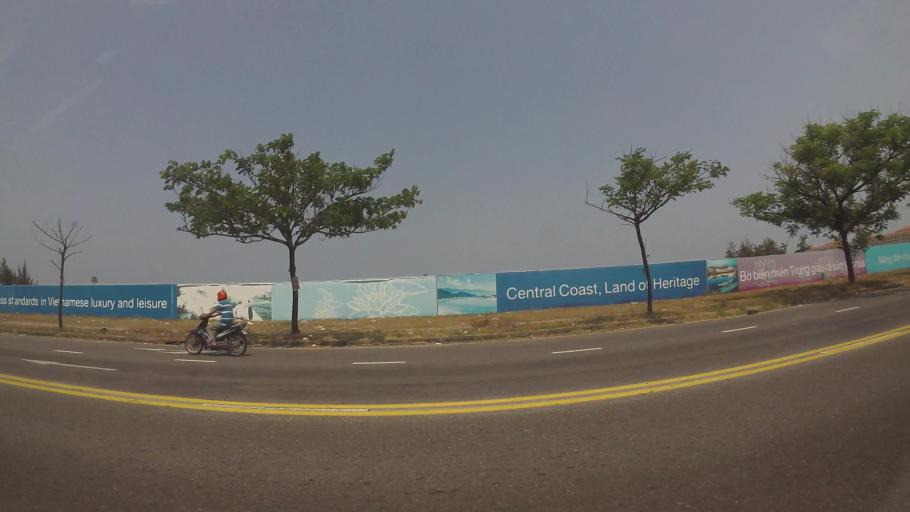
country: VN
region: Da Nang
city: Ngu Hanh Son
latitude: 15.9842
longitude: 108.2739
